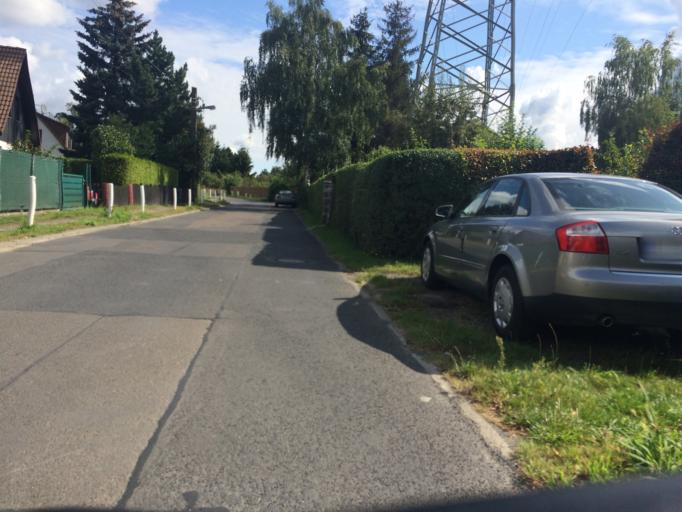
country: DE
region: Berlin
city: Weissensee
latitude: 52.5675
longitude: 13.4556
